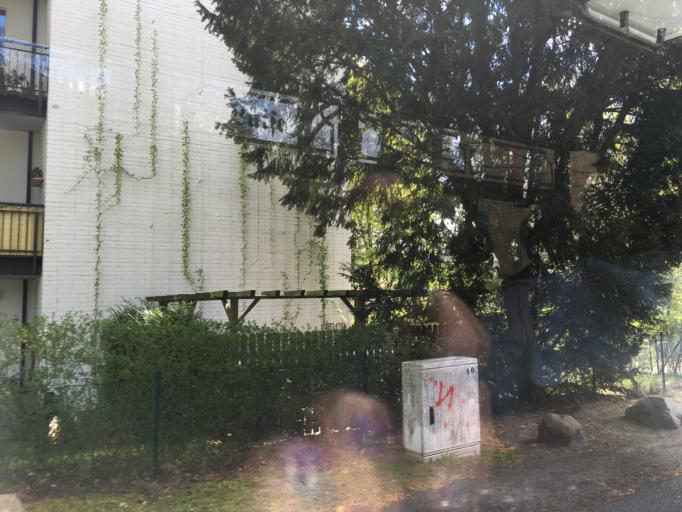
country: DE
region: Brandenburg
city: Potsdam
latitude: 52.4180
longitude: 13.0640
